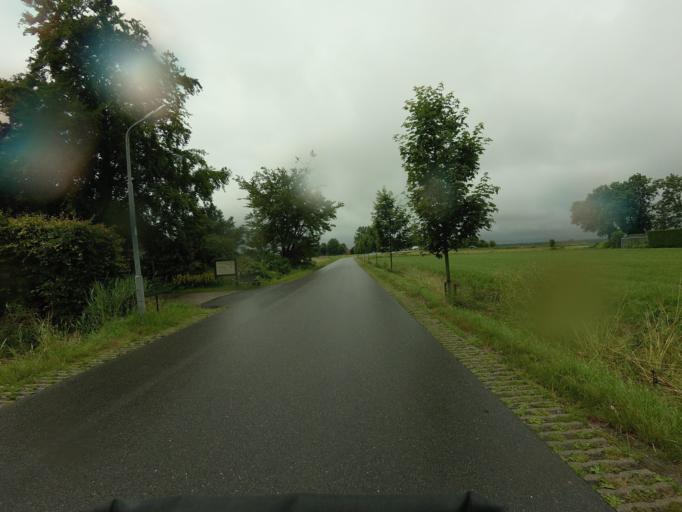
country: NL
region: North Holland
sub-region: Gemeente Opmeer
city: Opmeer
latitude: 52.7328
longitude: 4.9253
